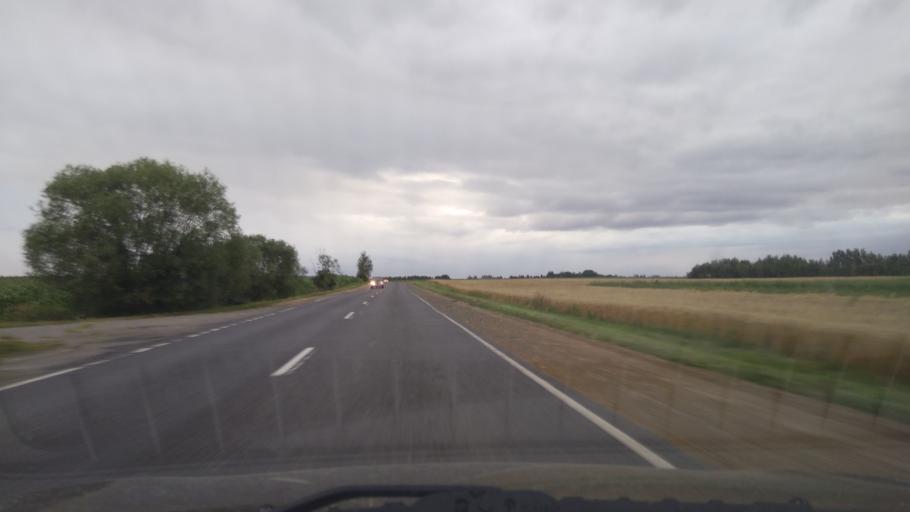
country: BY
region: Brest
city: Byaroza
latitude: 52.4283
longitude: 24.9807
